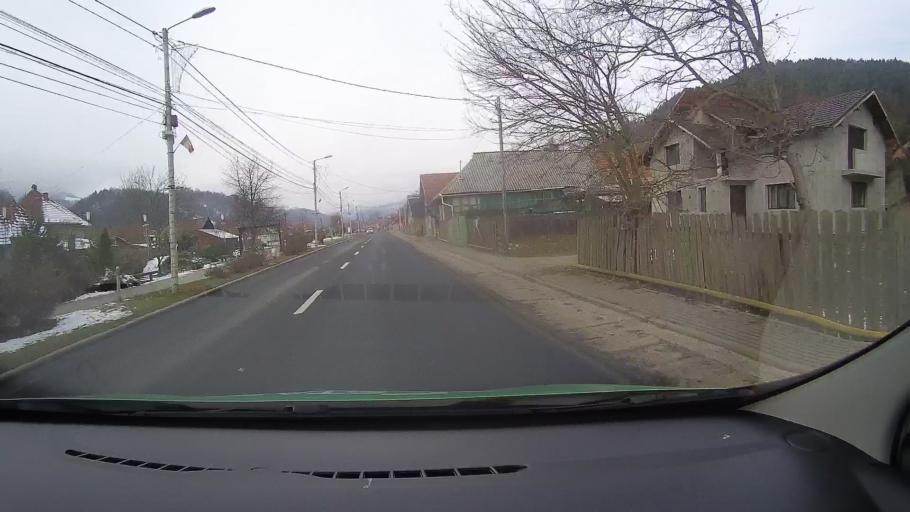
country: RO
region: Alba
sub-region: Oras Zlatna
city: Zlatna
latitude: 46.1126
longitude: 23.2182
